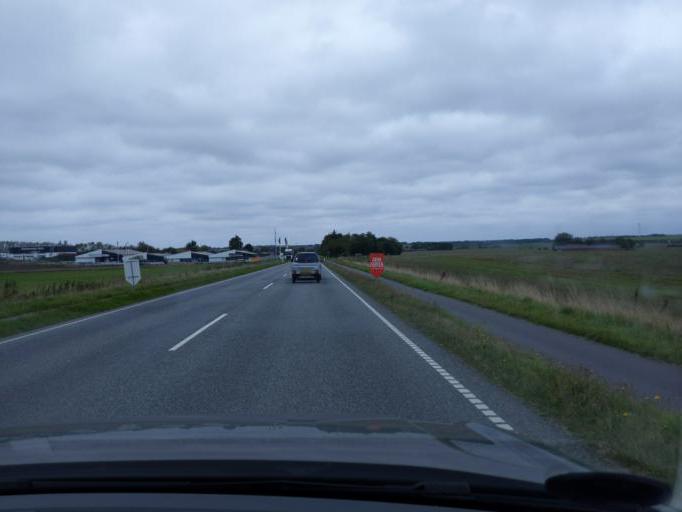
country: DK
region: Central Jutland
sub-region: Randers Kommune
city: Spentrup
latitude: 56.5044
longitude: 9.9596
